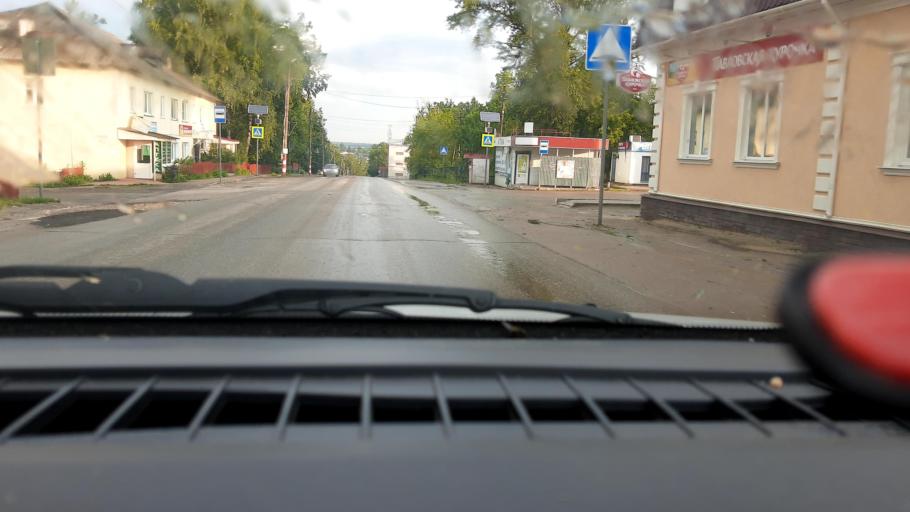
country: RU
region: Nizjnij Novgorod
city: Lukoyanov
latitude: 55.0360
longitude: 44.4945
